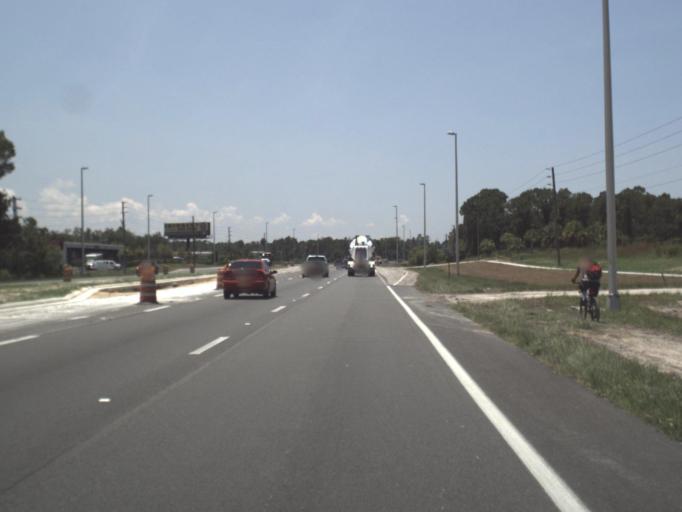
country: US
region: Florida
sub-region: Hernando County
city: Hernando Beach
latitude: 28.4110
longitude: -82.6511
